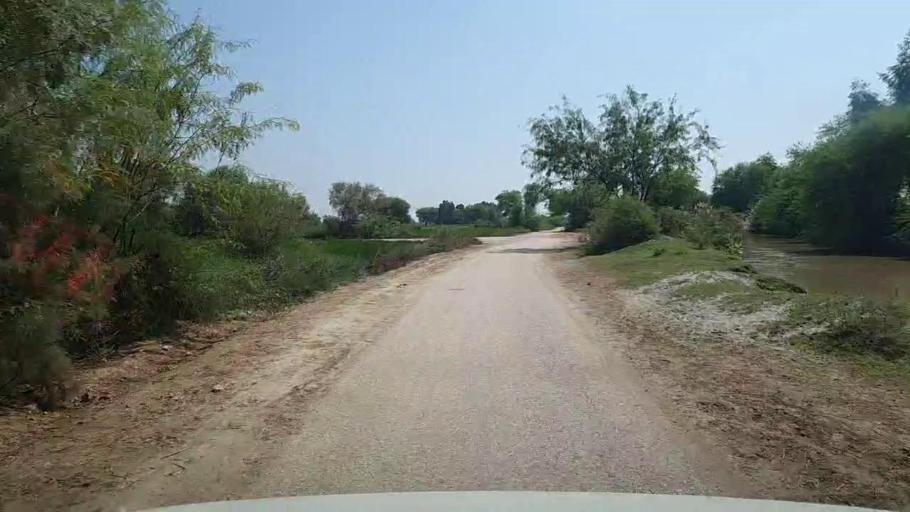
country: PK
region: Sindh
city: Kandhkot
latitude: 28.2839
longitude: 69.3543
